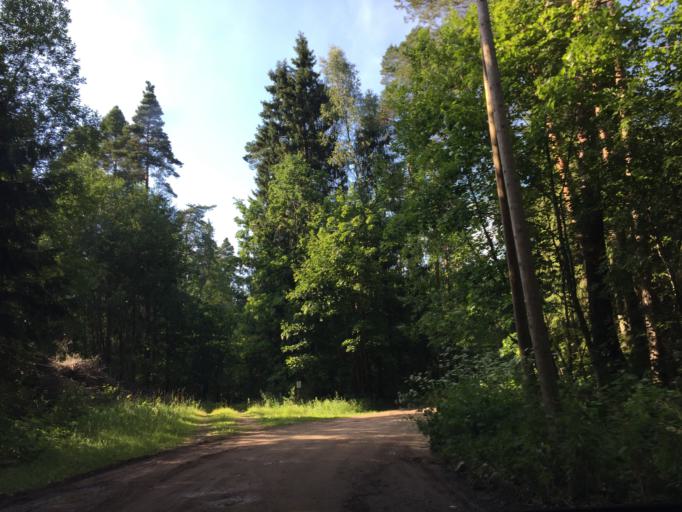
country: LV
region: Krimulda
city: Ragana
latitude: 57.1370
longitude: 24.7680
